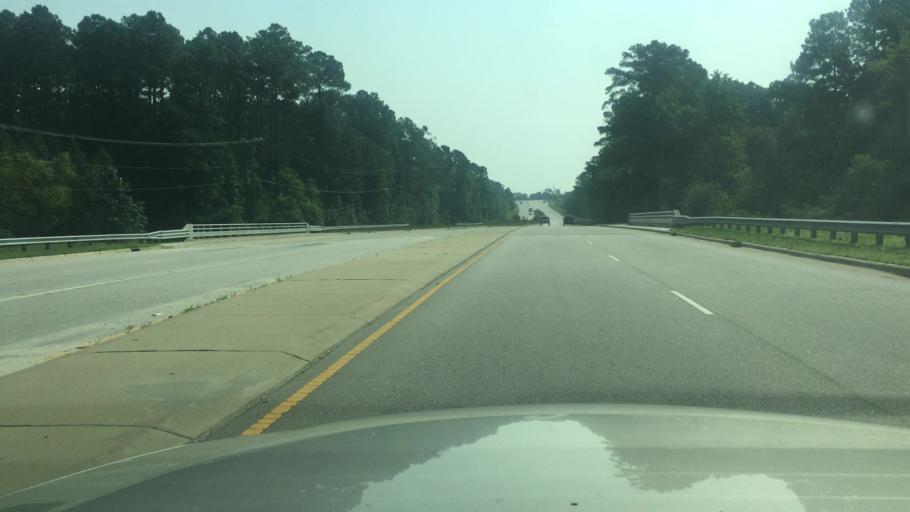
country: US
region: North Carolina
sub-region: Cumberland County
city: Hope Mills
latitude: 34.9875
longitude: -78.9570
